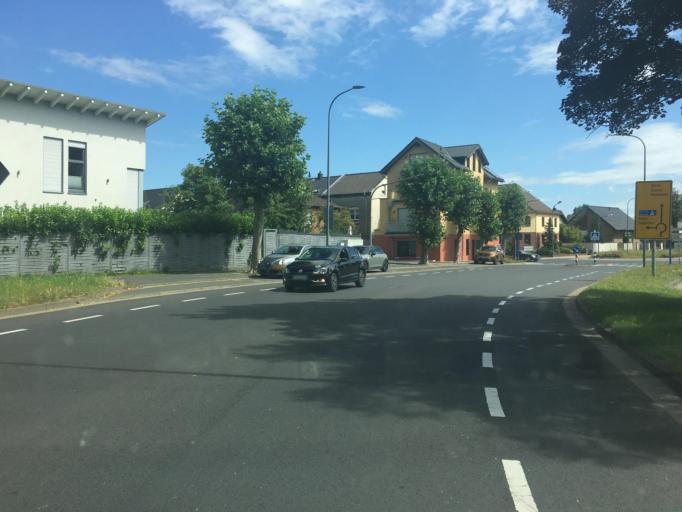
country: DE
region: North Rhine-Westphalia
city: Zulpich
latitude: 50.6943
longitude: 6.6517
